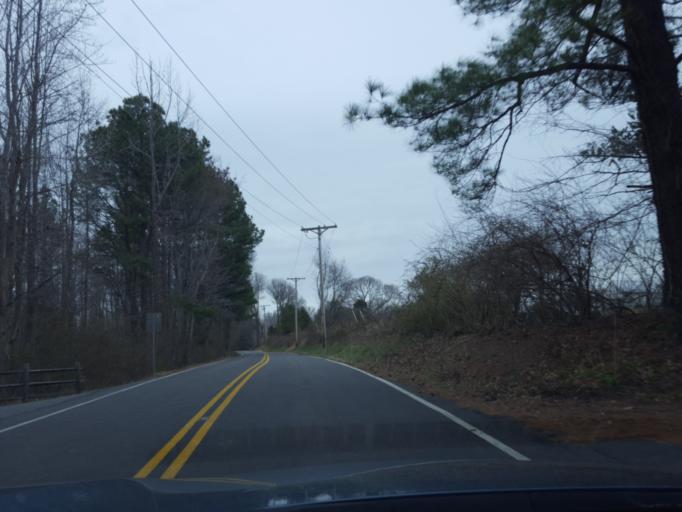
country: US
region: Maryland
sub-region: Calvert County
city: Prince Frederick
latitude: 38.4905
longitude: -76.5897
